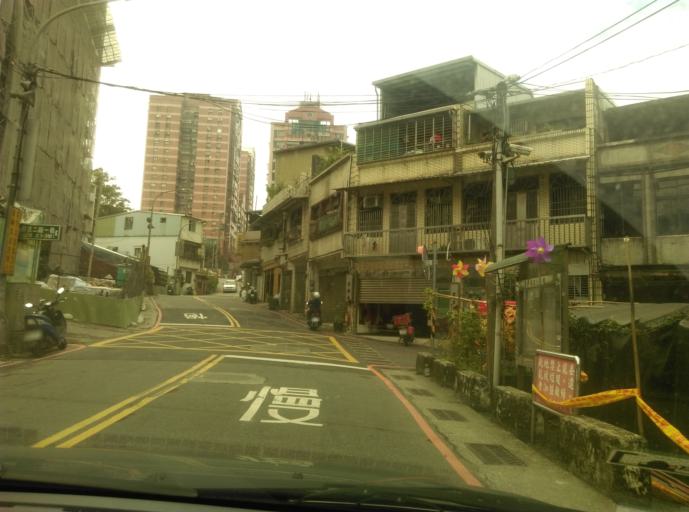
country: TW
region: Taiwan
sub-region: Keelung
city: Keelung
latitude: 25.1420
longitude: 121.7028
